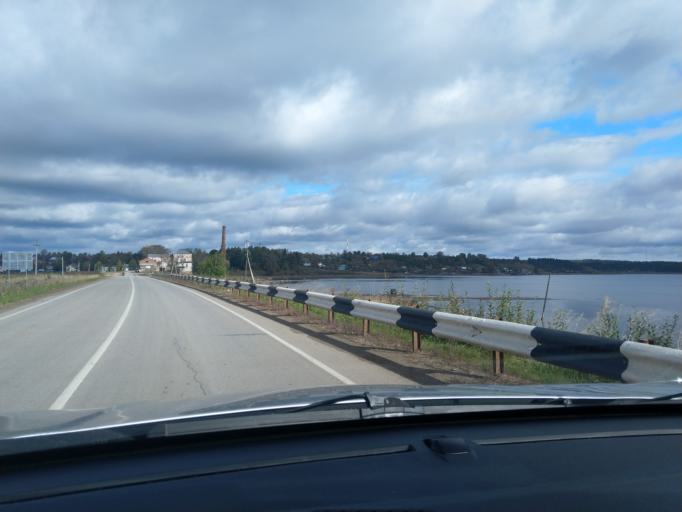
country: RU
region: Perm
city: Pozhva
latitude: 59.0799
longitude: 56.0805
